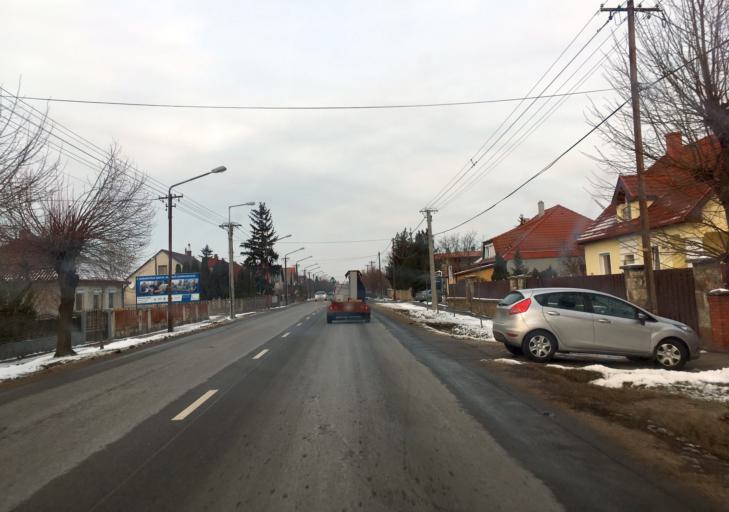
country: HU
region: Gyor-Moson-Sopron
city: Mosonmagyarovar
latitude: 47.8610
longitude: 17.2668
